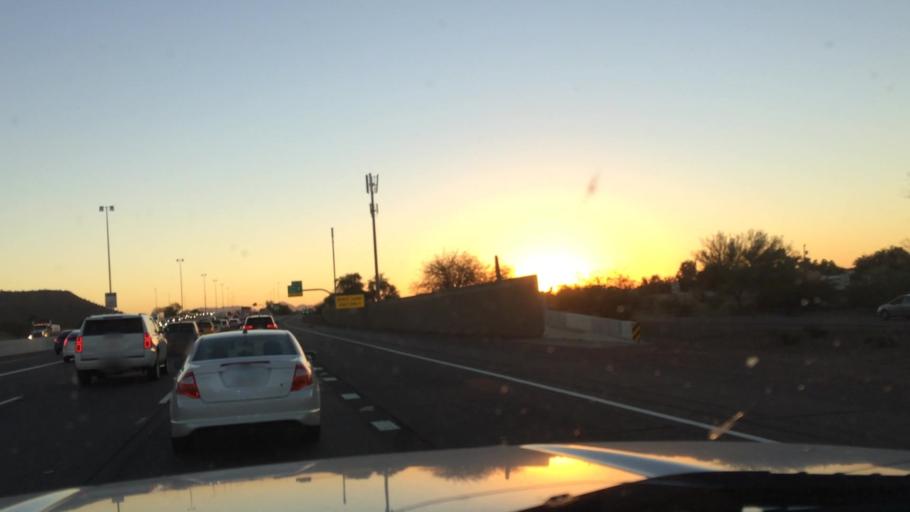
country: US
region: Arizona
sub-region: Maricopa County
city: Peoria
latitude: 33.6681
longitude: -112.1766
